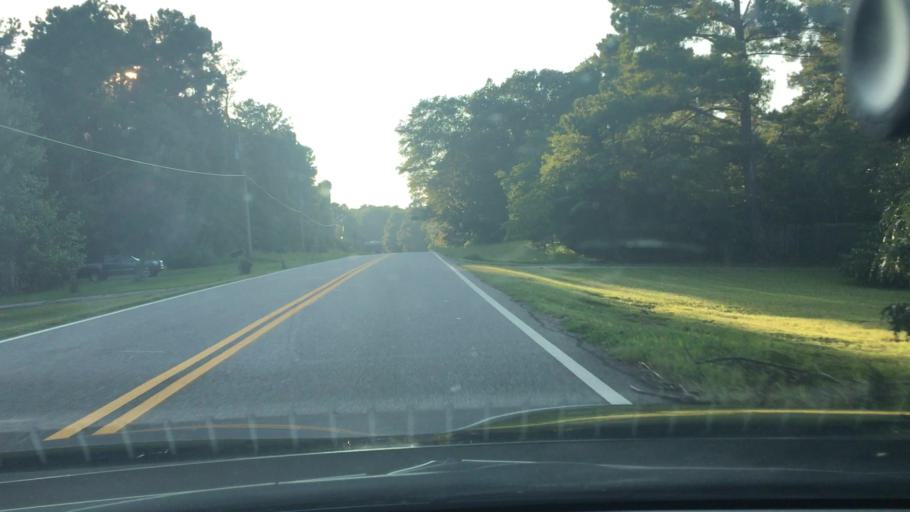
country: US
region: Georgia
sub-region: Coweta County
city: East Newnan
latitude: 33.3496
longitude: -84.7562
